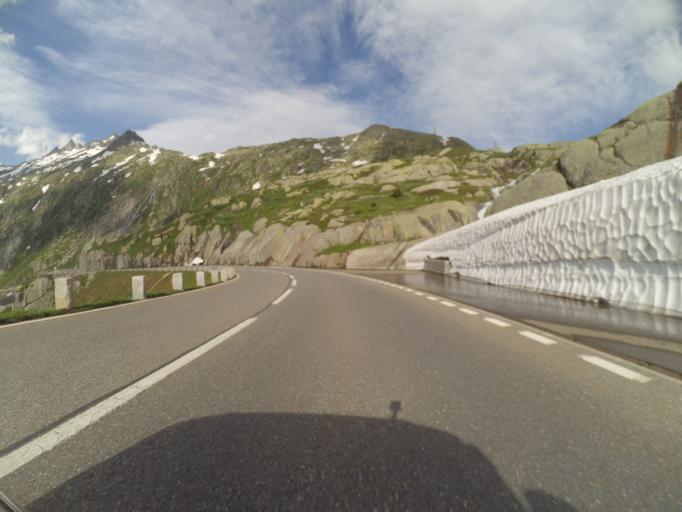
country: IT
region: Piedmont
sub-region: Provincia Verbano-Cusio-Ossola
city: Formazza
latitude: 46.5654
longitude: 8.3350
